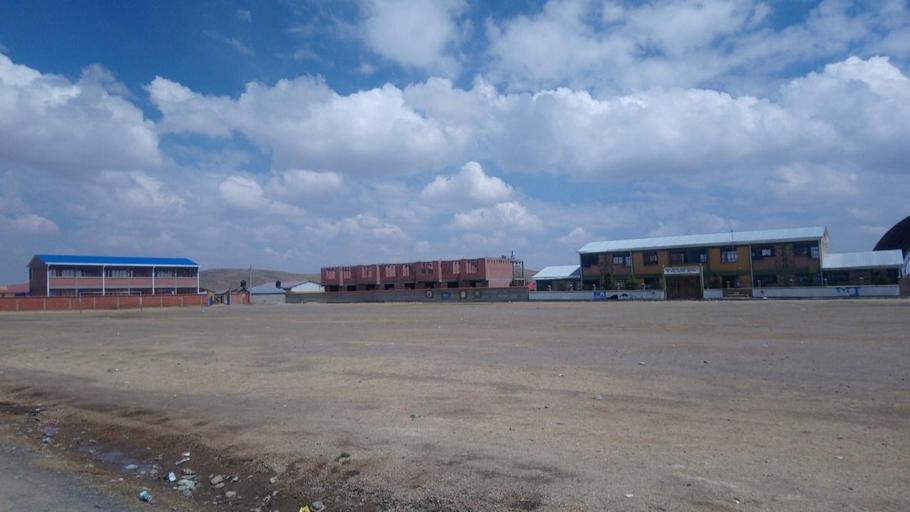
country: BO
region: La Paz
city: Batallas
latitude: -16.4092
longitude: -68.5412
